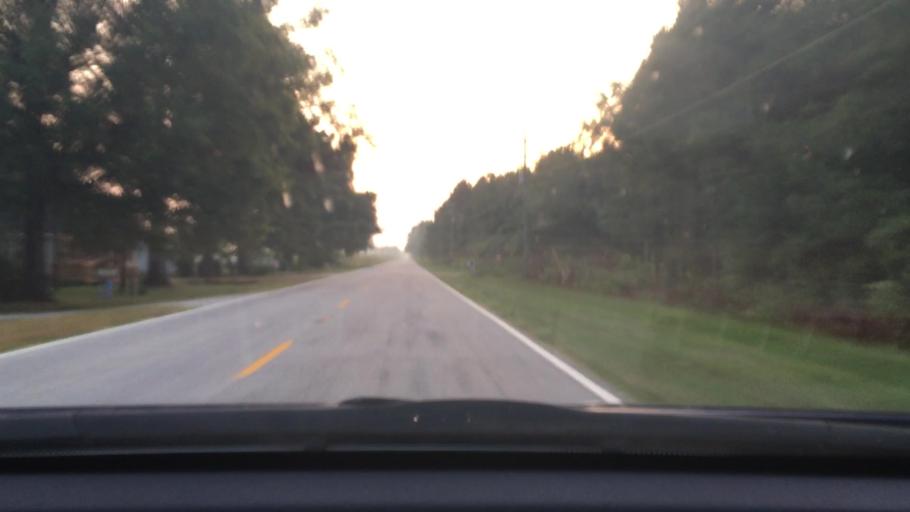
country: US
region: South Carolina
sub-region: Lee County
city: Bishopville
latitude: 34.1110
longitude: -80.1551
